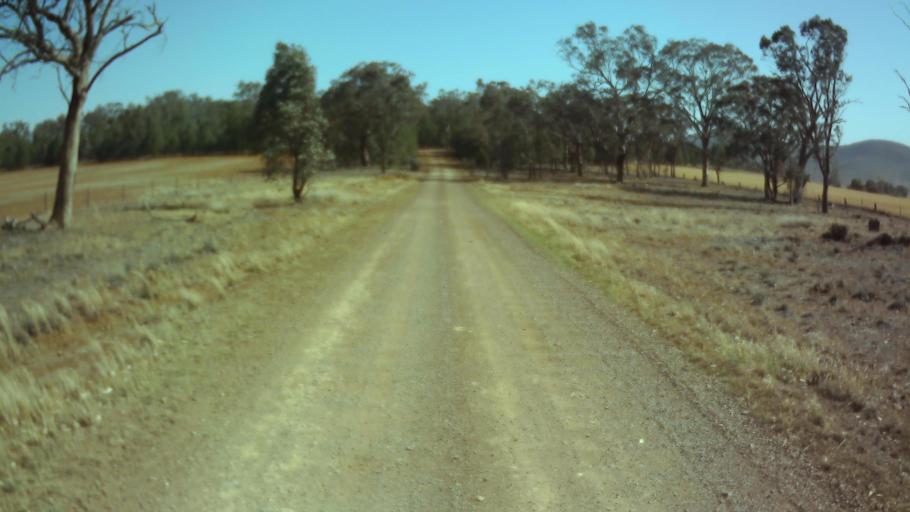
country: AU
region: New South Wales
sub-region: Weddin
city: Grenfell
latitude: -33.8593
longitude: 148.0153
